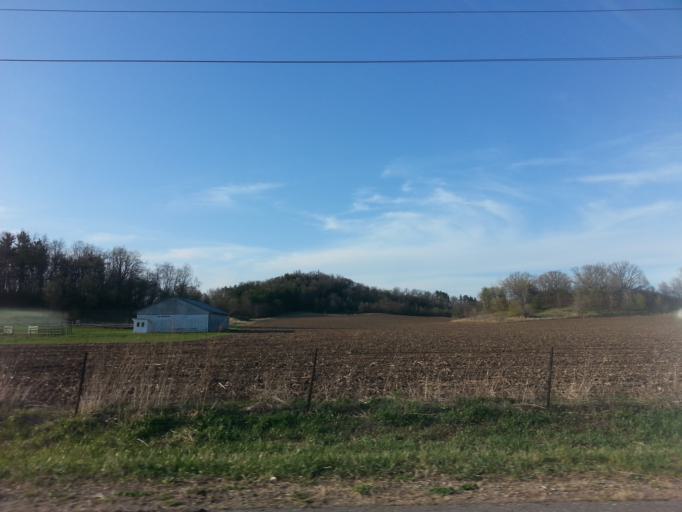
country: US
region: Minnesota
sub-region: Washington County
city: Afton
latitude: 44.8447
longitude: -92.7239
